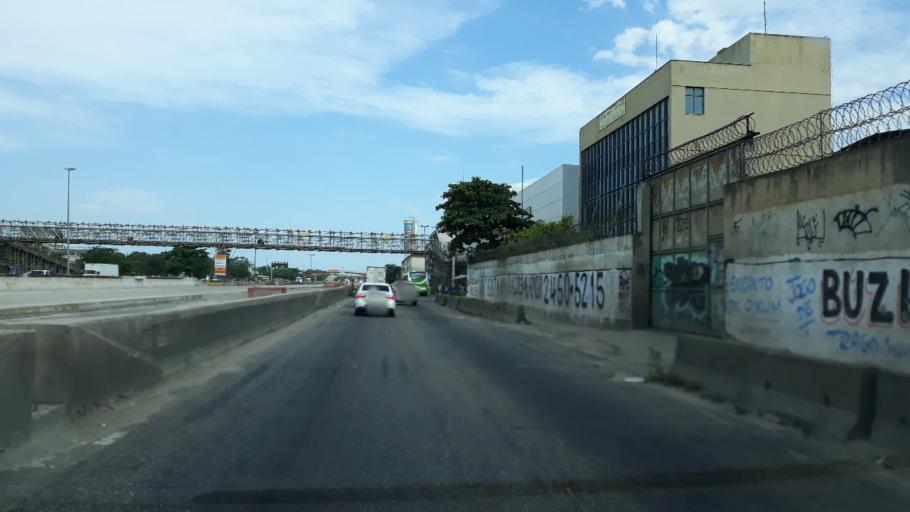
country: BR
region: Rio de Janeiro
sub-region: Duque De Caxias
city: Duque de Caxias
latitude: -22.8198
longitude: -43.2840
